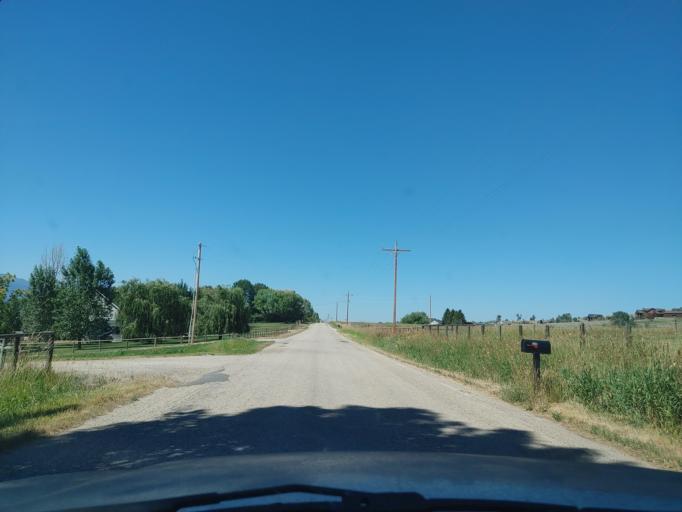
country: US
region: Montana
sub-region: Ravalli County
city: Hamilton
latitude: 46.3412
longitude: -114.0615
